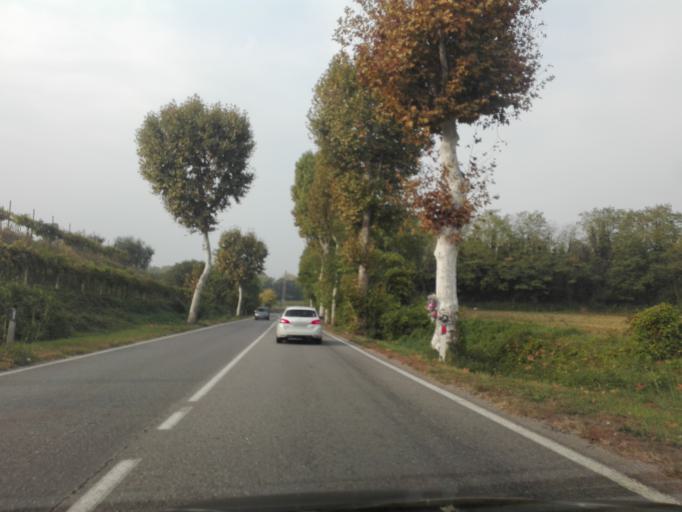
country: IT
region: Veneto
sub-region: Provincia di Verona
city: San Giorgio in Salici
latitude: 45.4403
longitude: 10.7898
